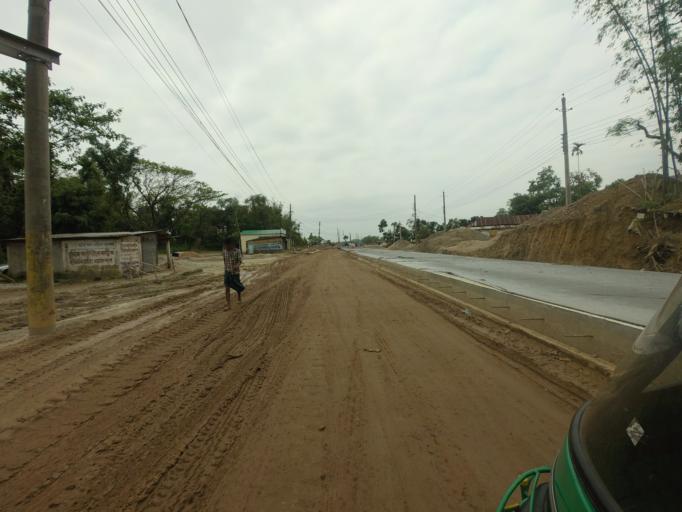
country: BD
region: Sylhet
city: Sylhet
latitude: 24.9664
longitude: 91.8692
